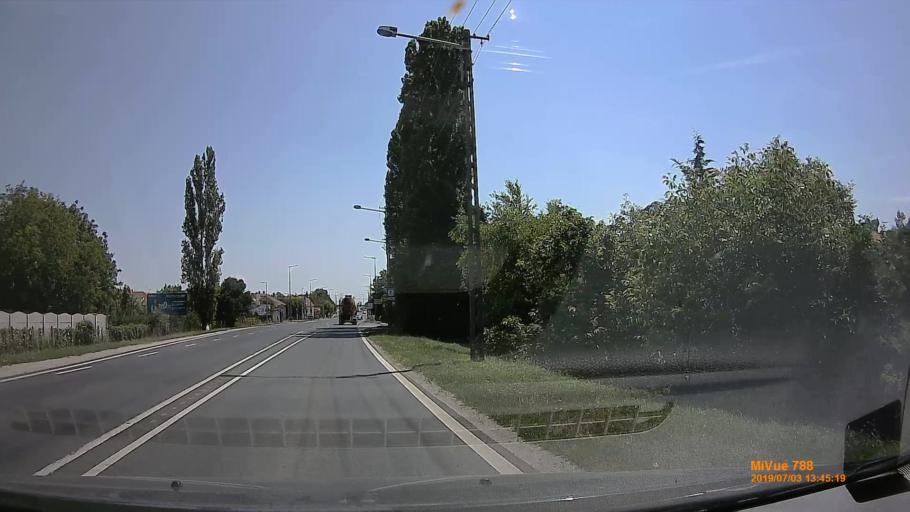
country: HU
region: Gyor-Moson-Sopron
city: Gyor
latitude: 47.7005
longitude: 17.6354
